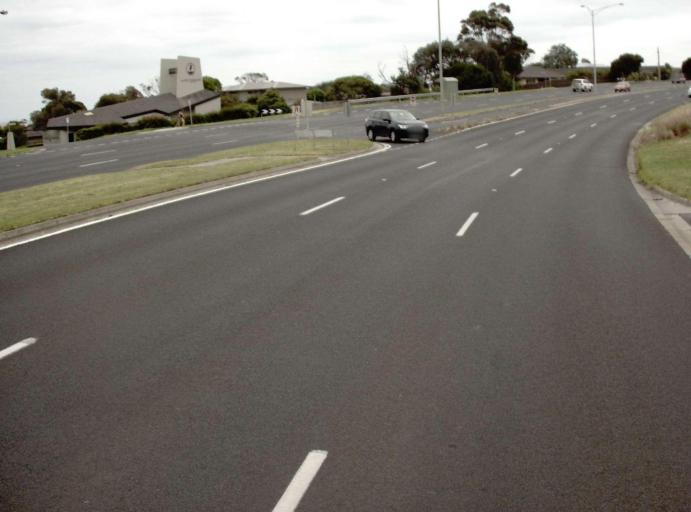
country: AU
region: Victoria
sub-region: Mornington Peninsula
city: Mornington
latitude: -38.2374
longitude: 145.0360
